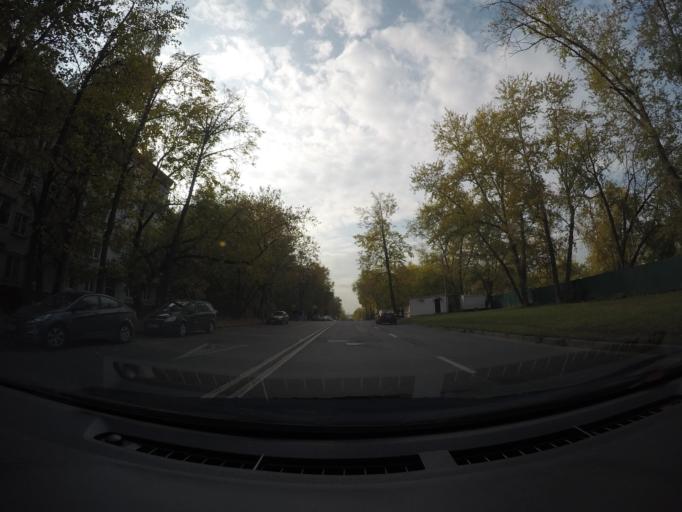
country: RU
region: Moscow
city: Lefortovo
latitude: 55.7684
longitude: 37.7402
